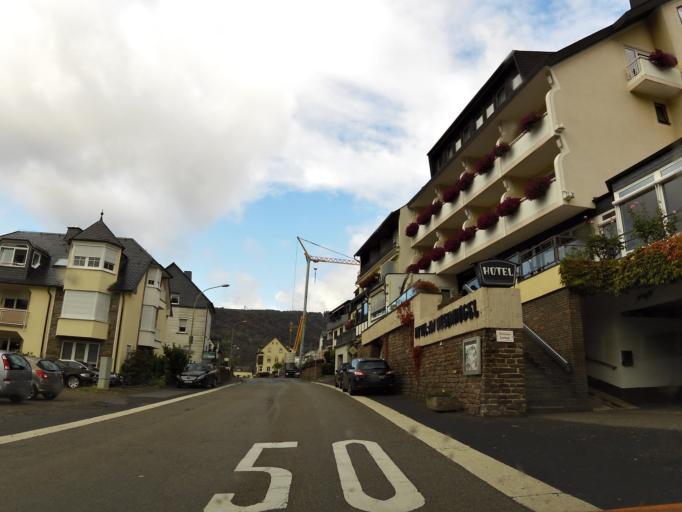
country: DE
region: Rheinland-Pfalz
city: Cochem
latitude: 50.1435
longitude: 7.1722
